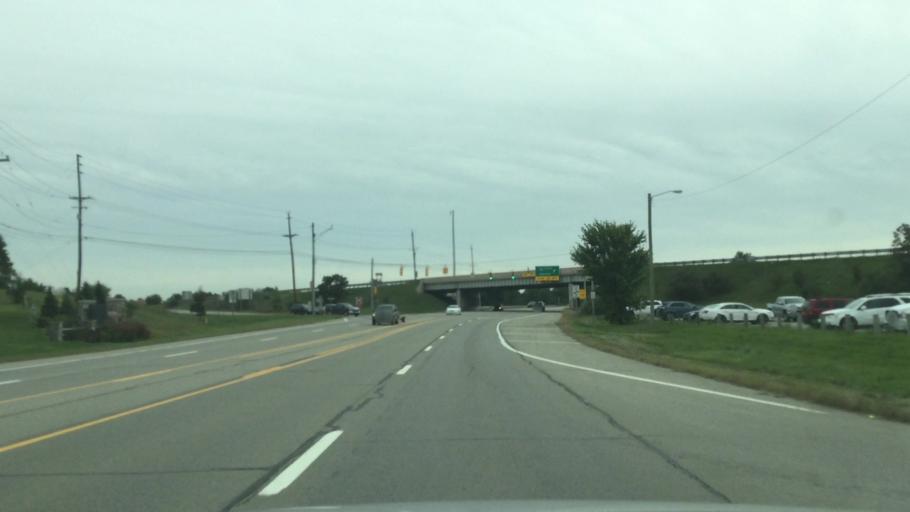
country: US
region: Michigan
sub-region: Oakland County
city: Clarkston
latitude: 42.7415
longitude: -83.4555
